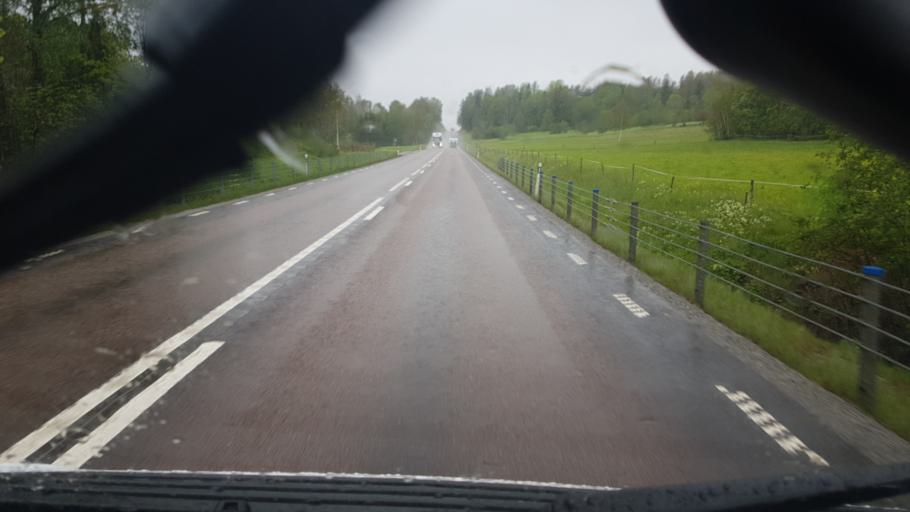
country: SE
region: Vaermland
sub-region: Arvika Kommun
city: Arvika
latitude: 59.6664
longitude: 12.8521
